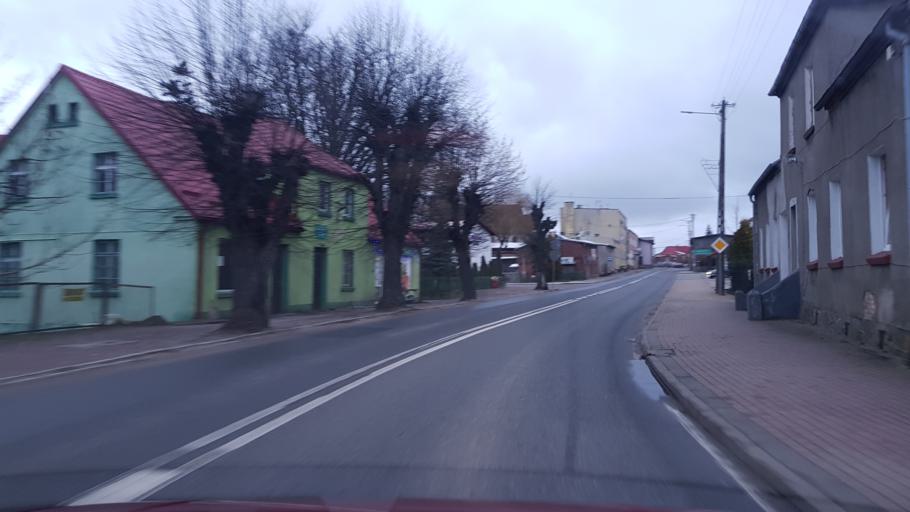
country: PL
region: Pomeranian Voivodeship
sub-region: Powiat bytowski
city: Tuchomie
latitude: 54.1138
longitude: 17.3347
